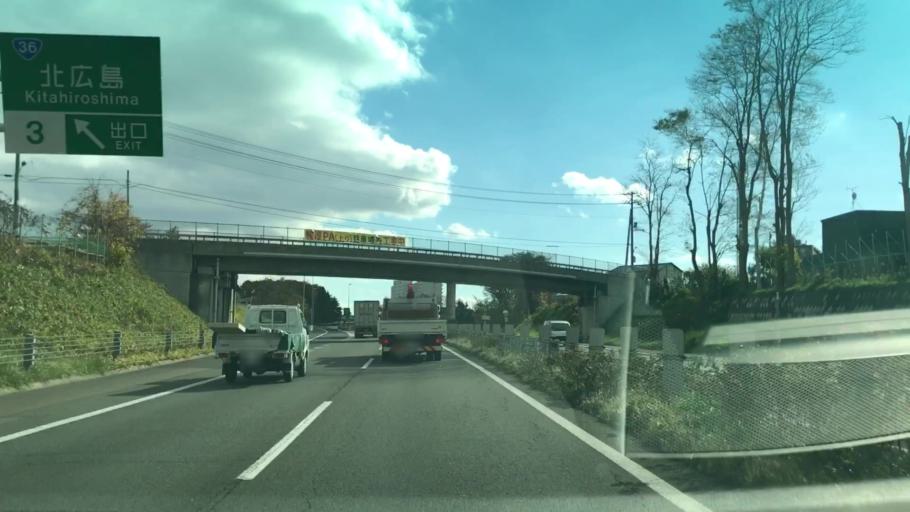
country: JP
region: Hokkaido
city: Kitahiroshima
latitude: 42.9805
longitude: 141.4747
